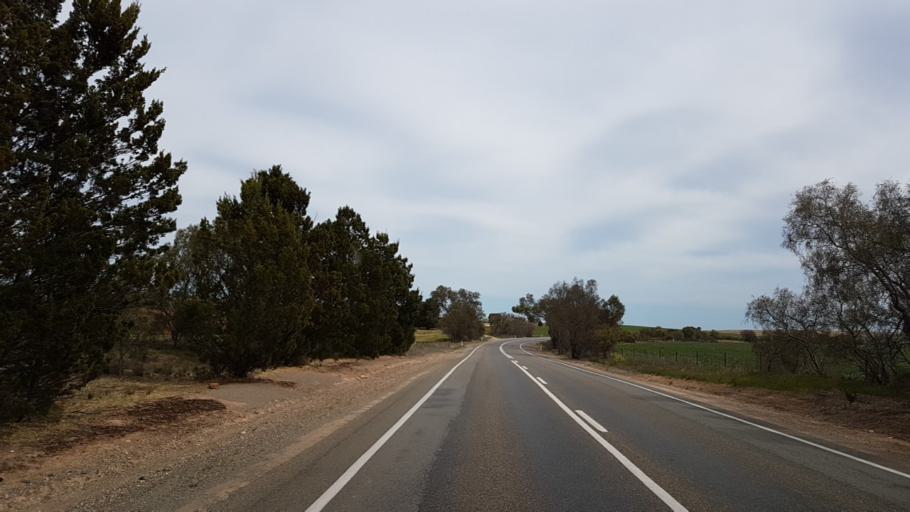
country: AU
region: South Australia
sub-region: Northern Areas
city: Jamestown
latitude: -33.2231
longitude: 138.4093
